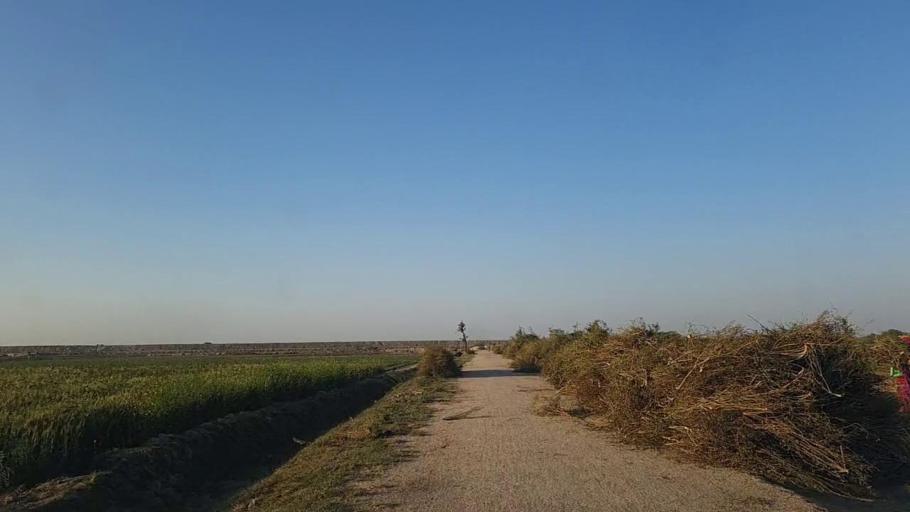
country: PK
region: Sindh
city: Naukot
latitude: 25.0056
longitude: 69.4266
